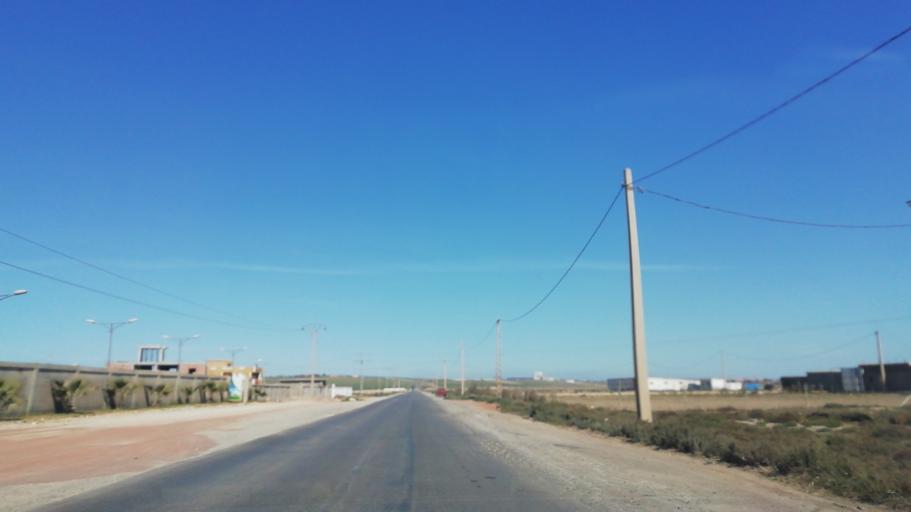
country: DZ
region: Oran
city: Es Senia
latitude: 35.5210
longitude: -0.5881
